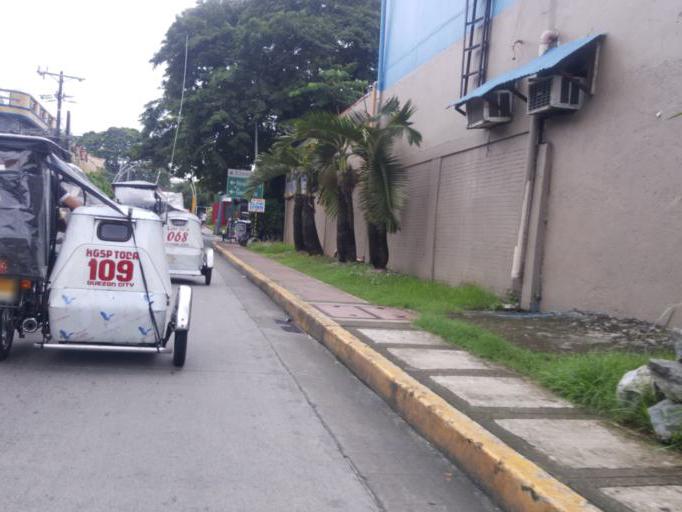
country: PH
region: Calabarzon
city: Bagong Pagasa
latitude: 14.6987
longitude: 121.0231
